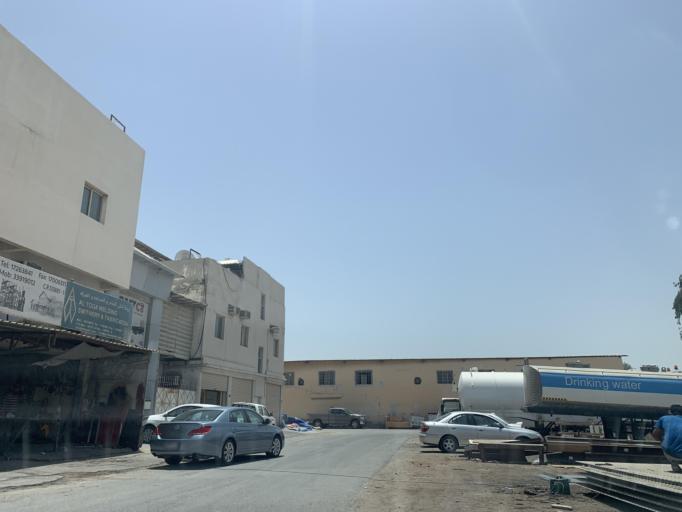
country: BH
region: Northern
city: Sitrah
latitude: 26.1553
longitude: 50.6222
